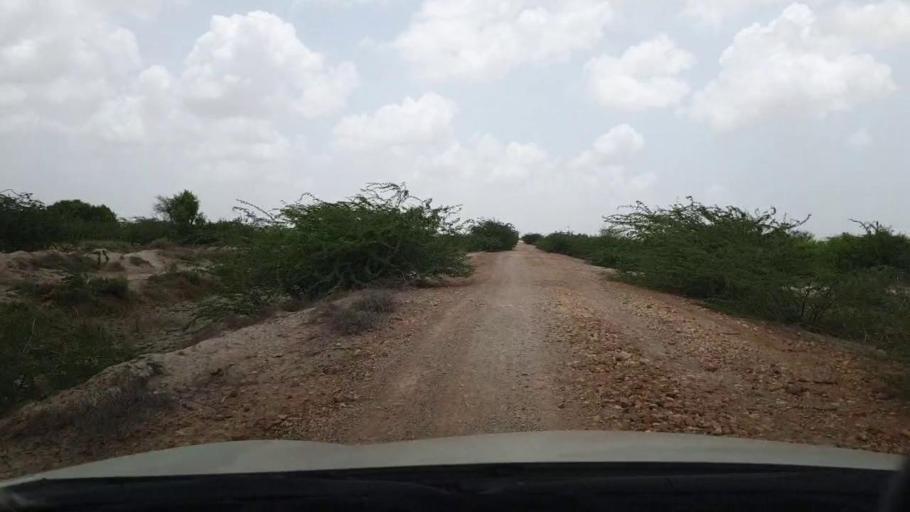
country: PK
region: Sindh
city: Kadhan
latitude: 24.3716
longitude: 68.9277
